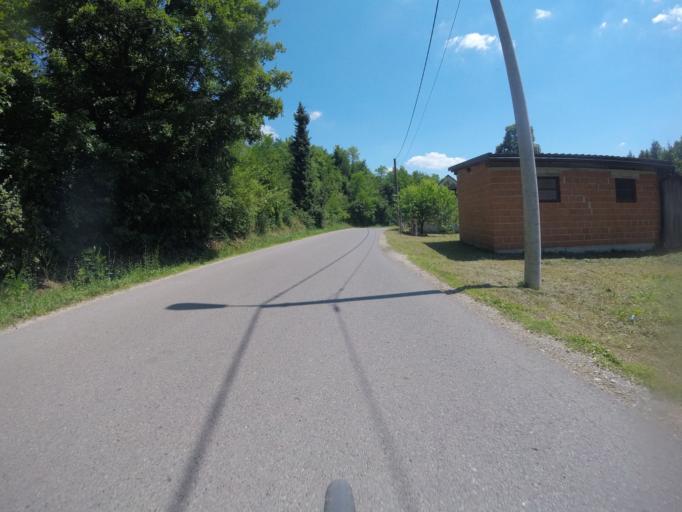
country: HR
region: Karlovacka
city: Ozalj
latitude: 45.6644
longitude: 15.4928
